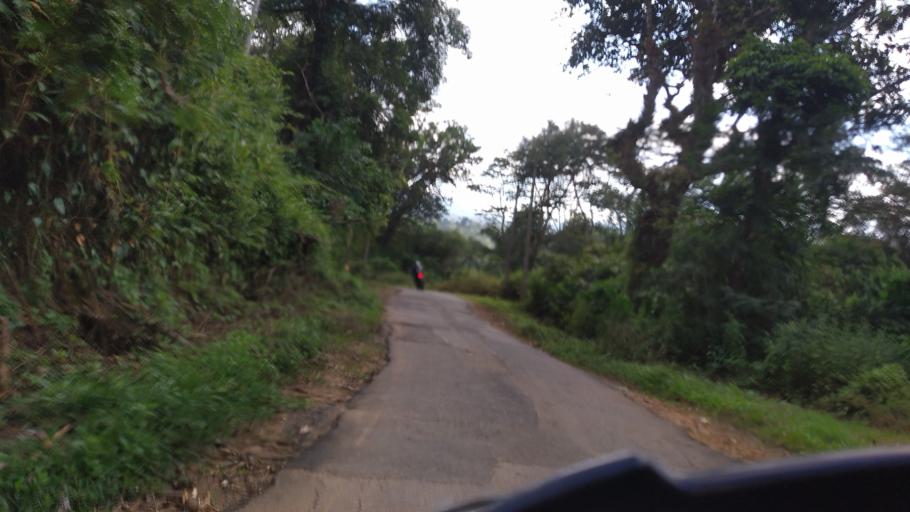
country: IN
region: Karnataka
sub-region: Kodagu
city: Ponnampet
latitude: 12.0355
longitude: 75.9104
